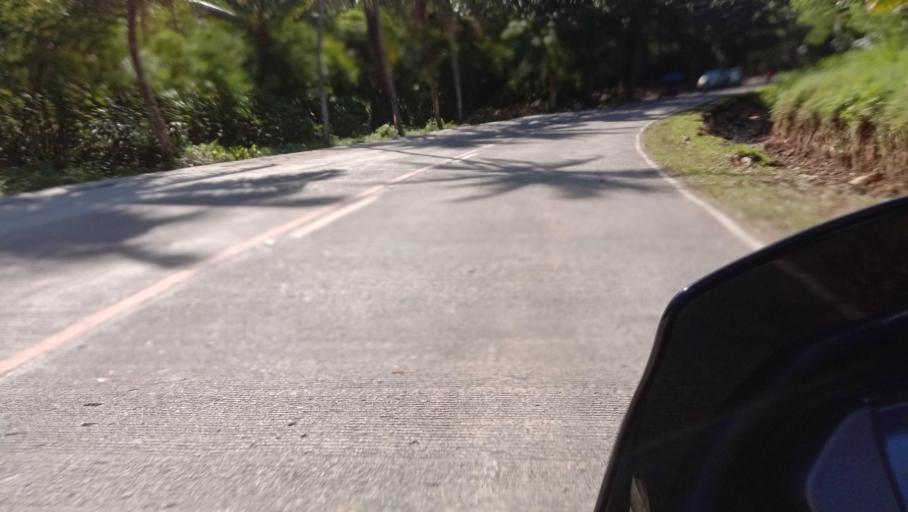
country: PH
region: Caraga
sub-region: Province of Surigao del Sur
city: Barobo
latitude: 8.5372
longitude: 126.1008
